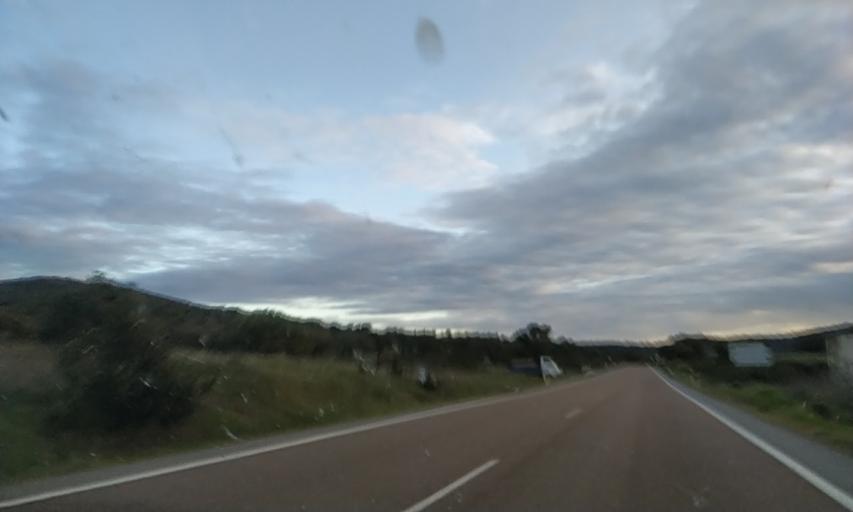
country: ES
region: Extremadura
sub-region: Provincia de Caceres
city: Malpartida de Caceres
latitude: 39.2979
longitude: -6.5182
